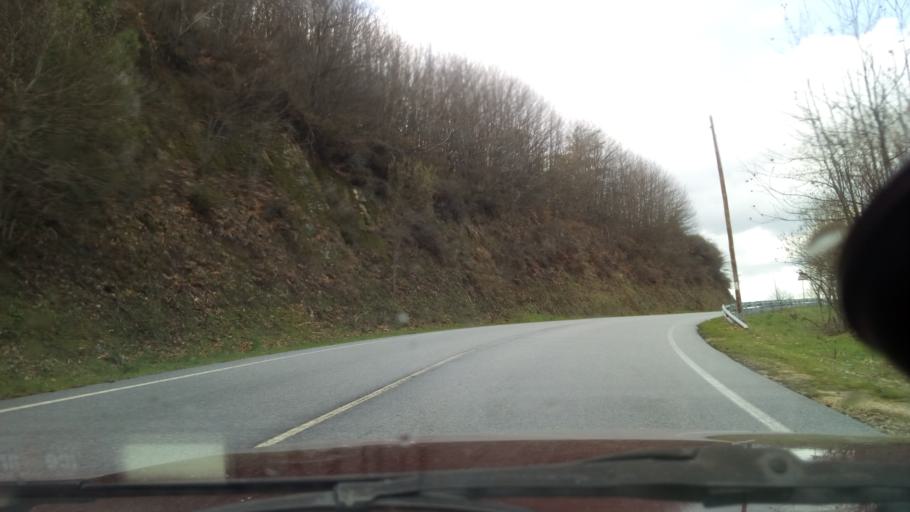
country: PT
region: Guarda
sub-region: Guarda
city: Guarda
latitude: 40.5489
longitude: -7.3151
